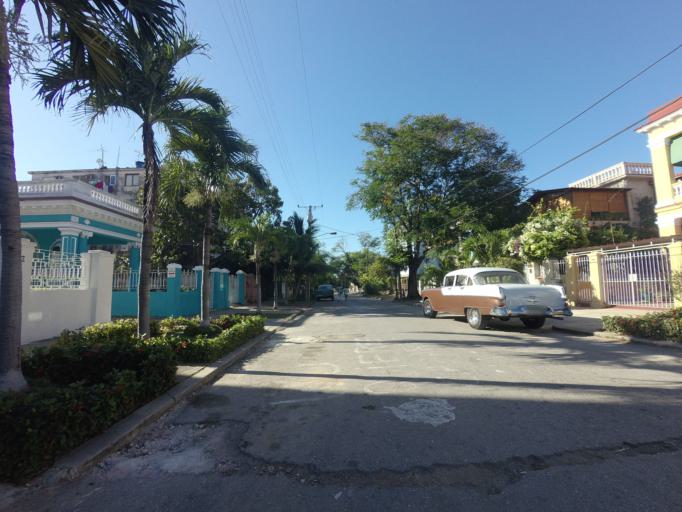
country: CU
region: La Habana
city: Havana
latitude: 23.1286
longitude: -82.4024
